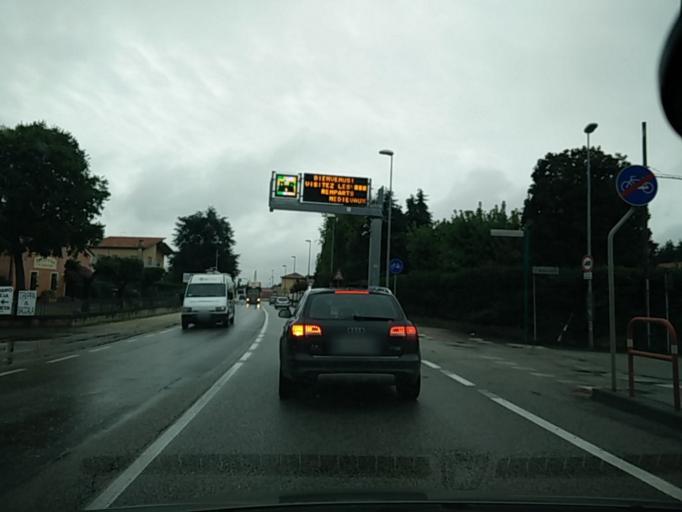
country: IT
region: Veneto
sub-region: Provincia di Vicenza
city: Belvedere
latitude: 45.6677
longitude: 11.7781
